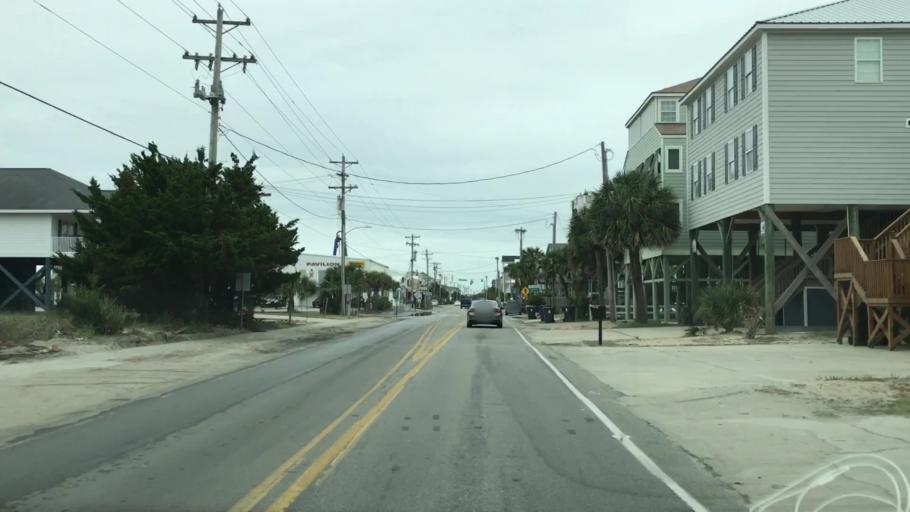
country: US
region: South Carolina
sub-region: Horry County
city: Garden City
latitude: 33.5756
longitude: -78.9997
